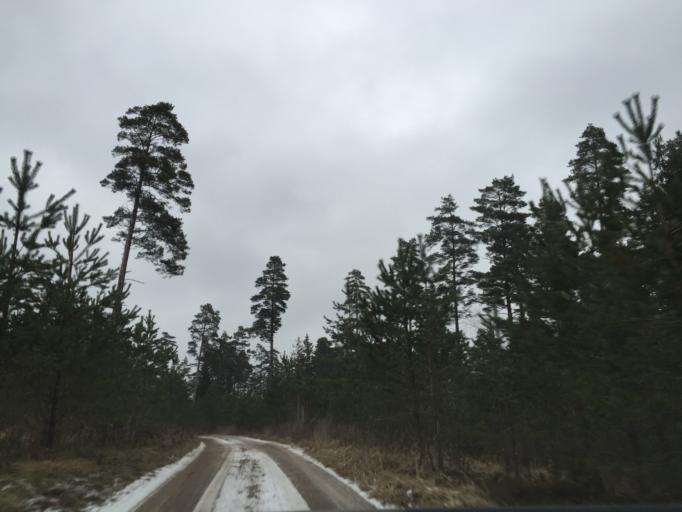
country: EE
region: Saare
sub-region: Kuressaare linn
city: Kuressaare
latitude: 58.3810
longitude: 22.2524
